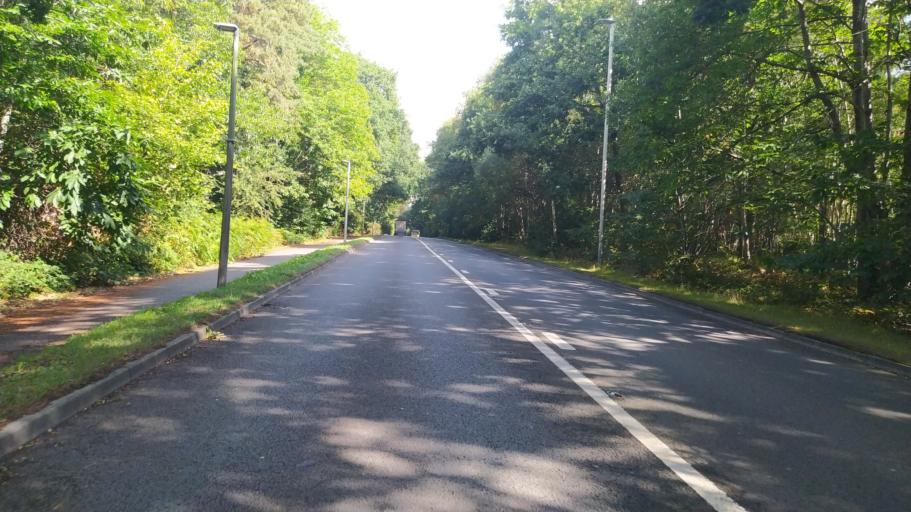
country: GB
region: England
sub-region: Dorset
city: Broadstone
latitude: 50.7577
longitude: -1.9810
